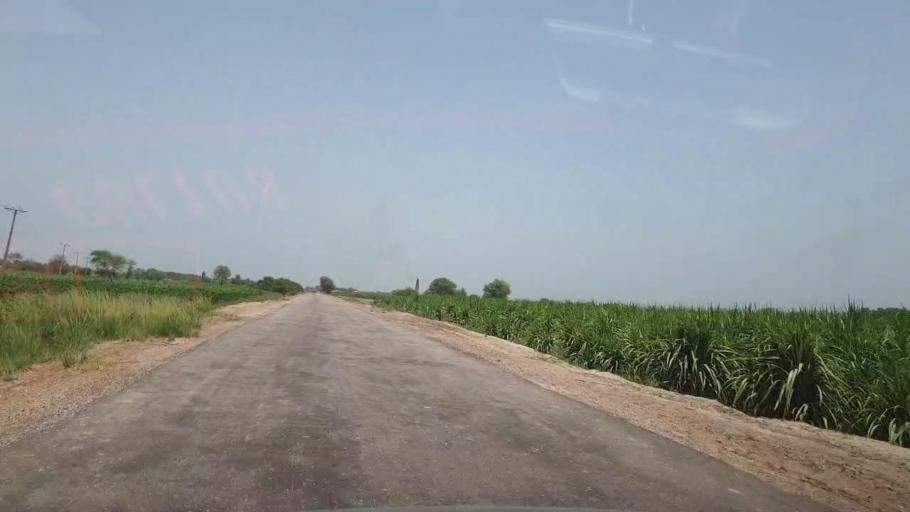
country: PK
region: Sindh
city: Daulatpur
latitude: 26.3894
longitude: 68.0843
